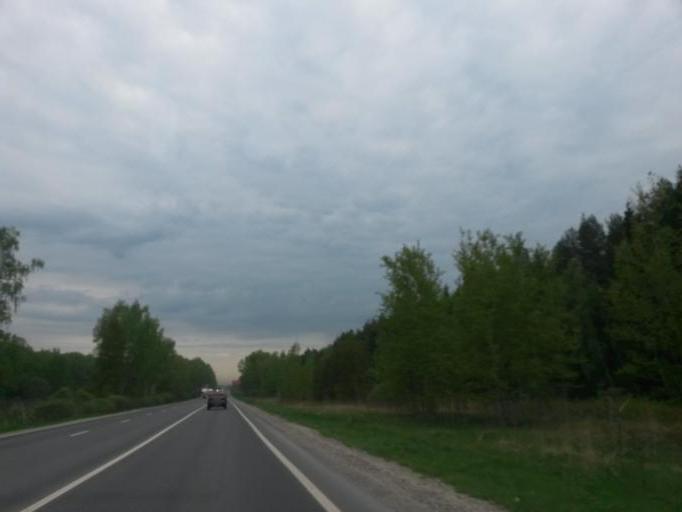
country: RU
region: Moskovskaya
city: Barybino
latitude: 55.2372
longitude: 37.8601
